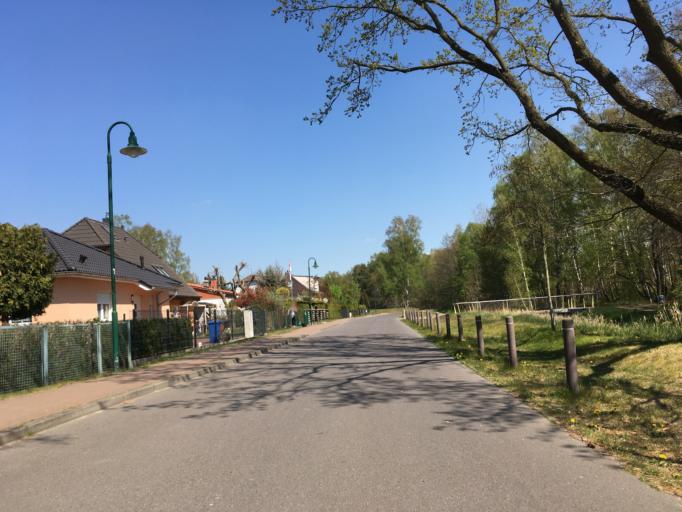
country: DE
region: Berlin
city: Buch
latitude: 52.6625
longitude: 13.5334
